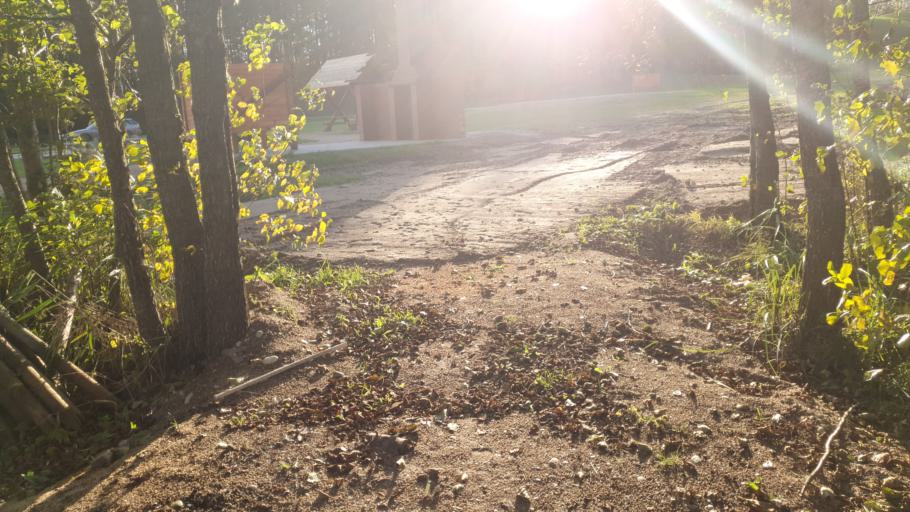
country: PL
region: Podlasie
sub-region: Suwalki
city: Suwalki
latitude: 54.2628
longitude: 22.8610
